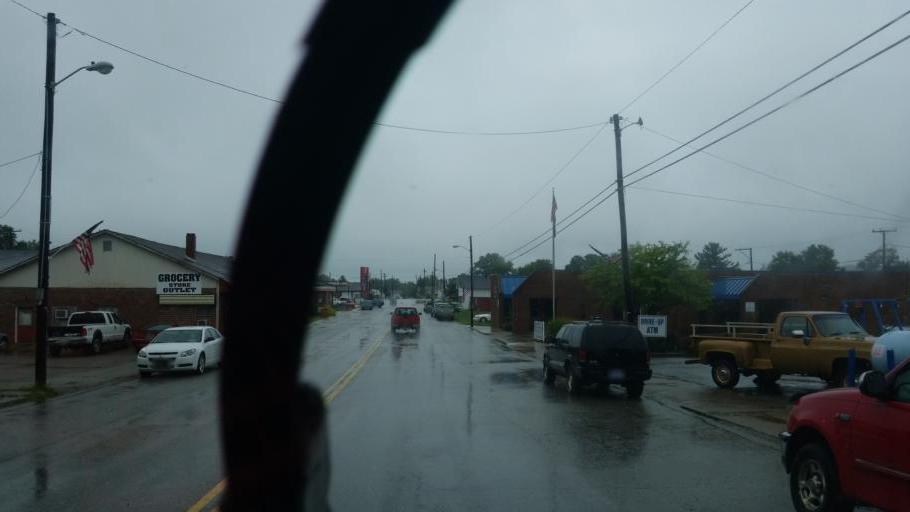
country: US
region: Kentucky
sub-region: Greenup County
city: South Shore
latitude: 38.7192
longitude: -82.9630
